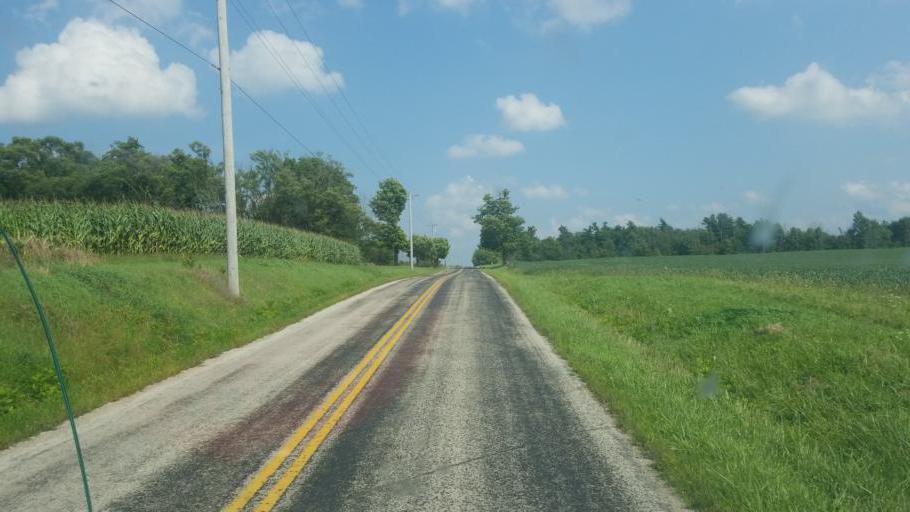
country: US
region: Ohio
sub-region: Lorain County
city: Wellington
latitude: 41.0576
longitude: -82.2674
